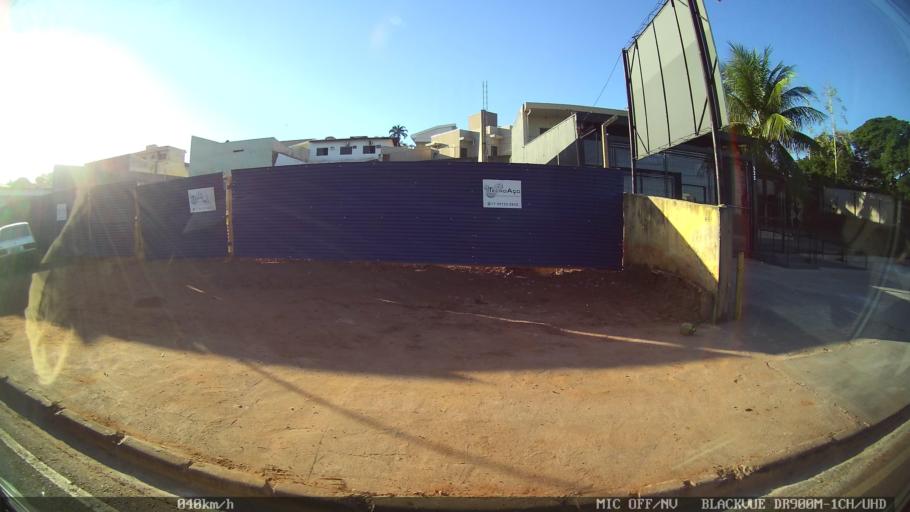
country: BR
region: Sao Paulo
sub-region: Sao Jose Do Rio Preto
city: Sao Jose do Rio Preto
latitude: -20.8084
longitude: -49.3687
